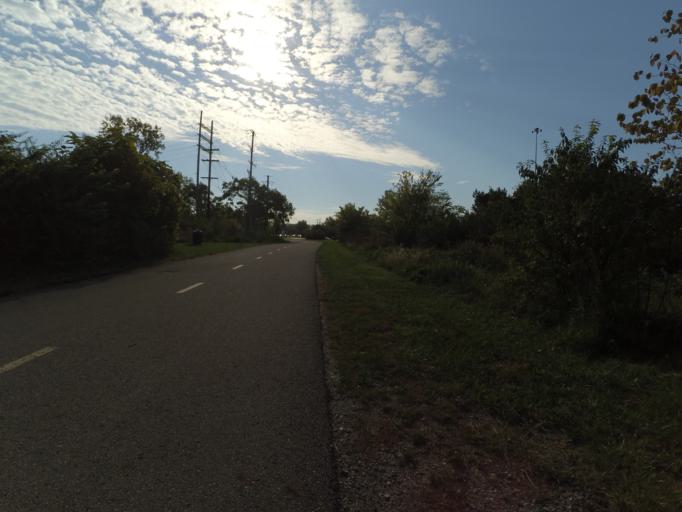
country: US
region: Ohio
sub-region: Franklin County
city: Columbus
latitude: 39.9671
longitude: -83.0206
